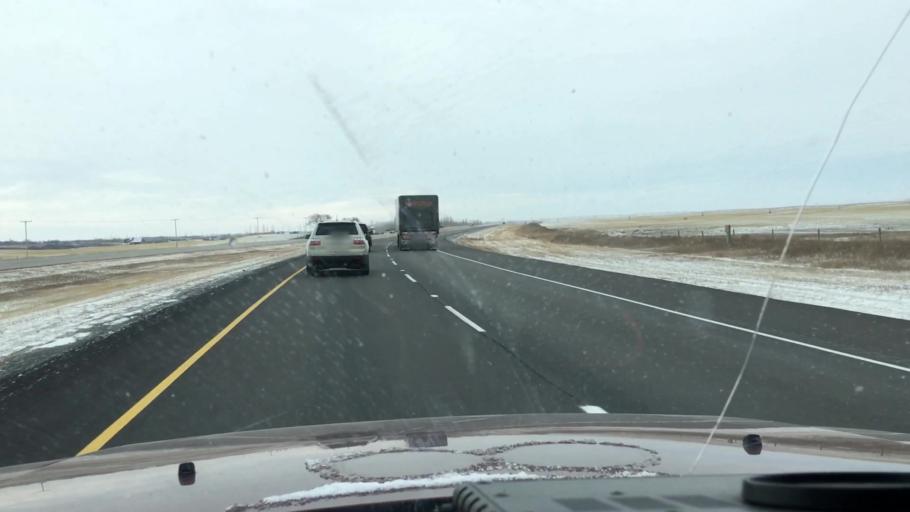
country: CA
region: Saskatchewan
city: Saskatoon
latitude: 51.7797
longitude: -106.4767
